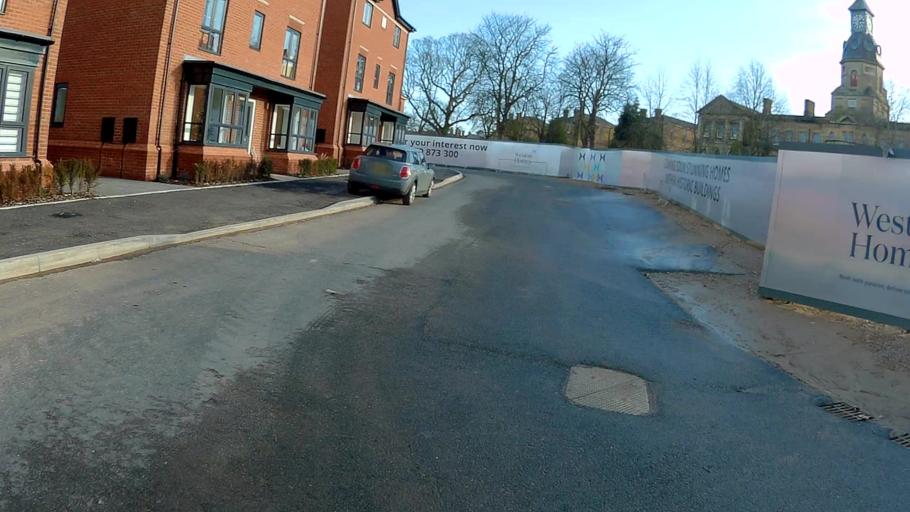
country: GB
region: England
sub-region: Hampshire
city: Aldershot
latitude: 51.2545
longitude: -0.7580
